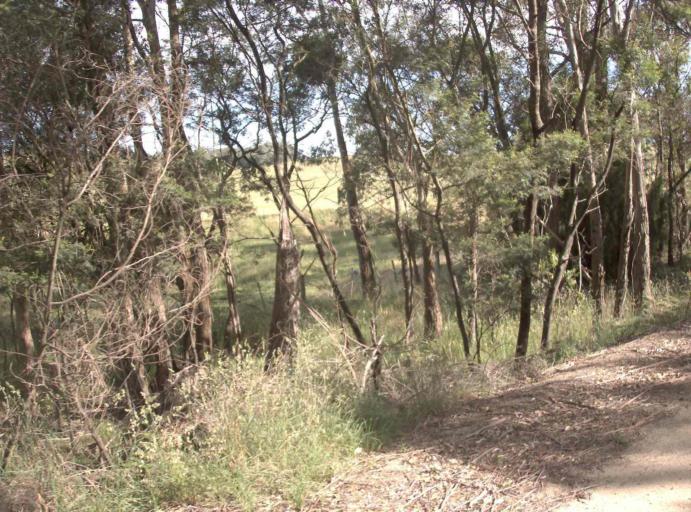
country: AU
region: Victoria
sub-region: East Gippsland
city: Lakes Entrance
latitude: -37.5359
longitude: 148.1485
